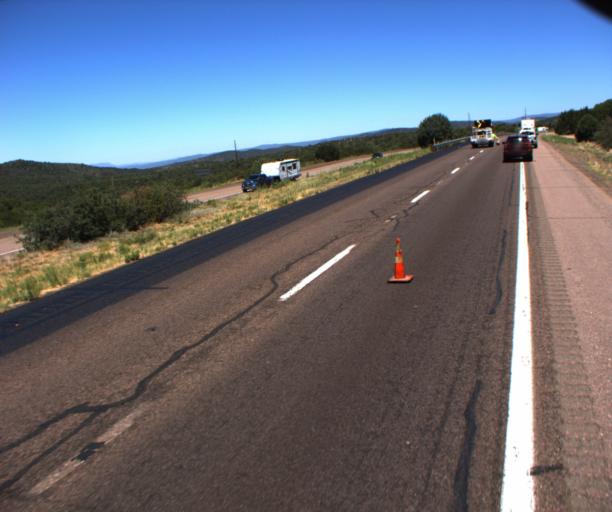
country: US
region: Arizona
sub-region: Gila County
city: Payson
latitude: 34.1717
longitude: -111.3368
